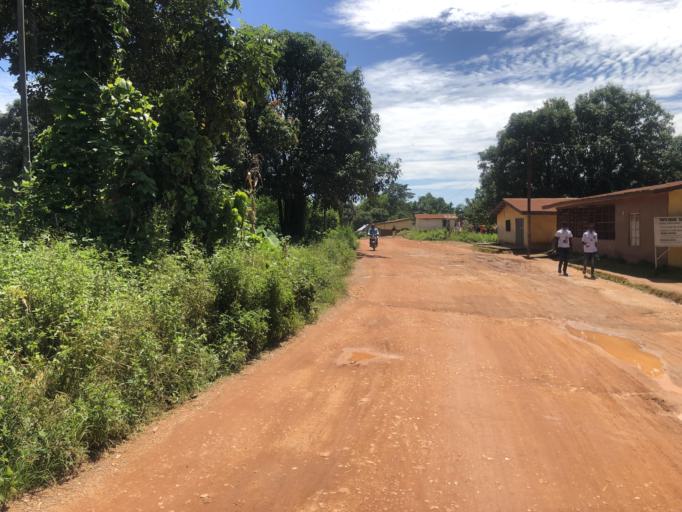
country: SL
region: Eastern Province
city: Koidu
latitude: 8.6406
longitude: -10.9661
